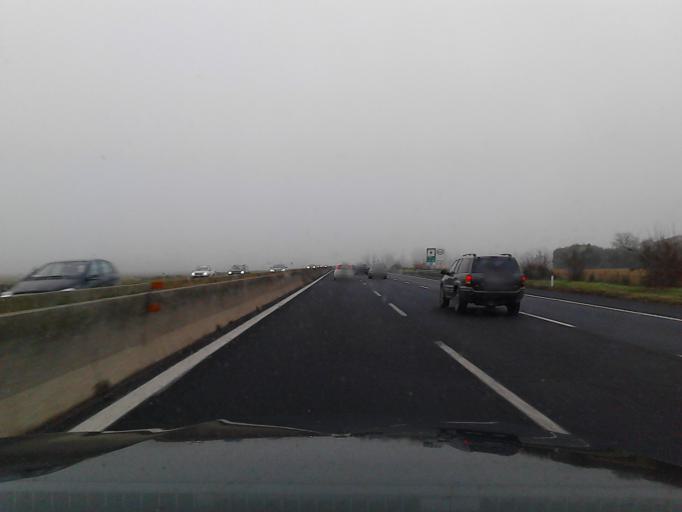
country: IT
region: Emilia-Romagna
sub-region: Provincia di Bologna
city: Toscanella
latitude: 44.4132
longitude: 11.6438
